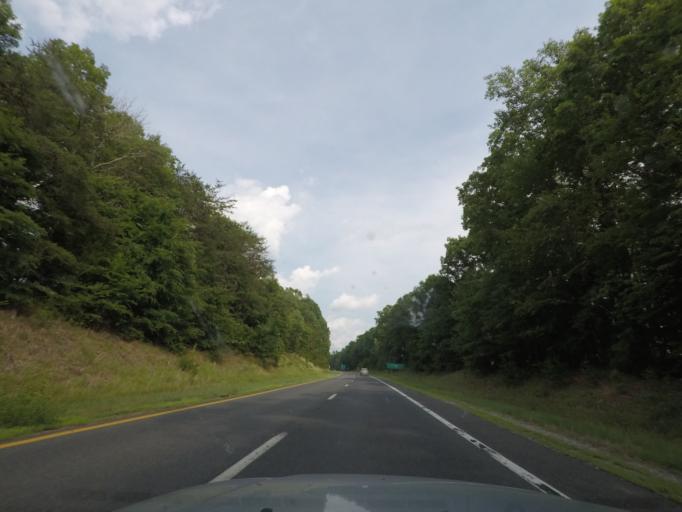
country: US
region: Virginia
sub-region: Prince Edward County
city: Farmville
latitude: 37.2717
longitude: -78.4161
